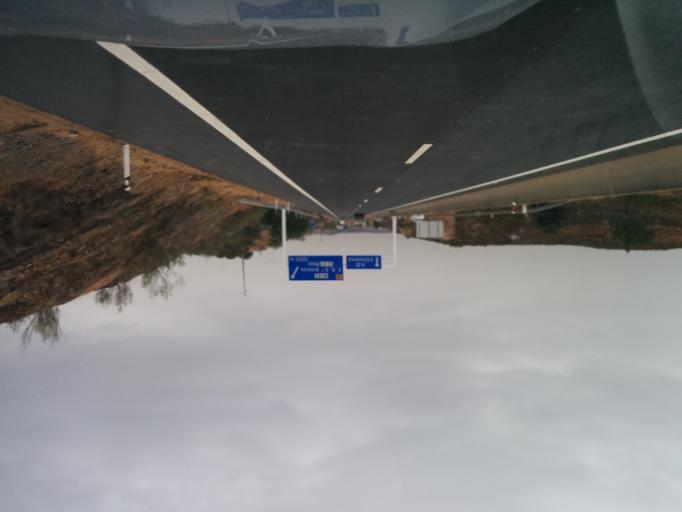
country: PT
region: Faro
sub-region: Castro Marim
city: Castro Marim
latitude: 37.2296
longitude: -7.4622
